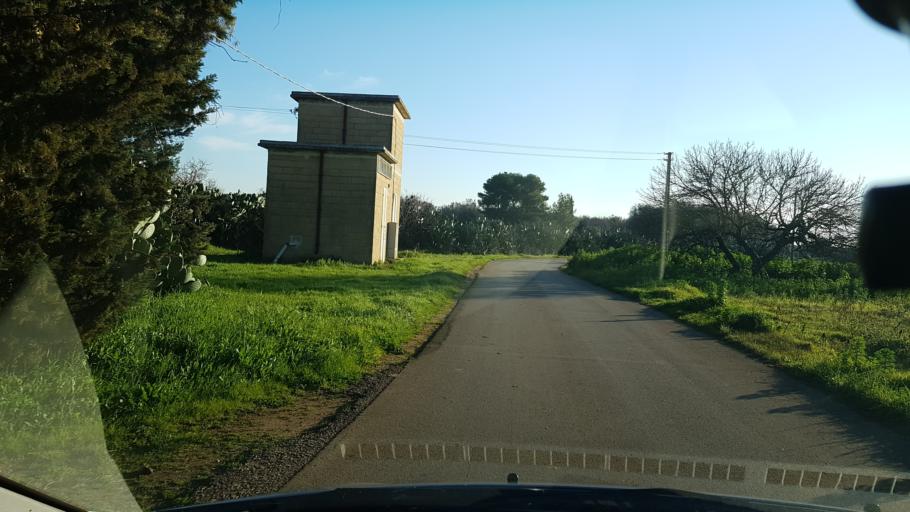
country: IT
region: Apulia
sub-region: Provincia di Brindisi
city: Mesagne
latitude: 40.5720
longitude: 17.8718
